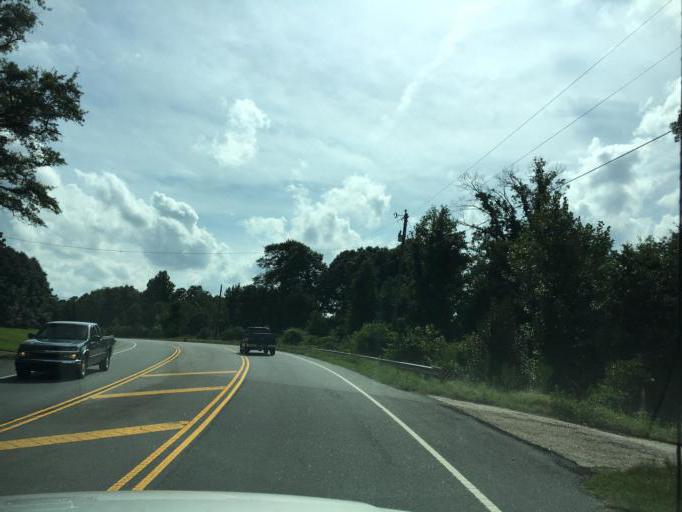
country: US
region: South Carolina
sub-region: Greenville County
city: Five Forks
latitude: 34.8492
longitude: -82.2352
